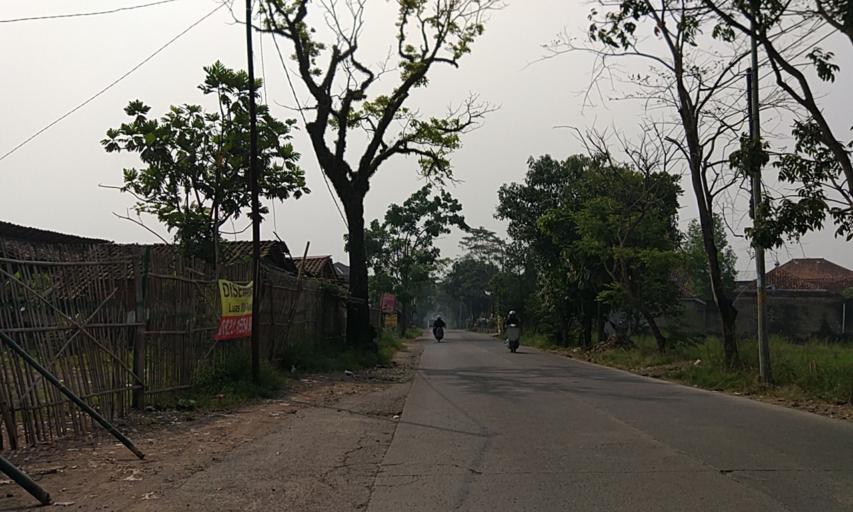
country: ID
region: West Java
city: Soreang
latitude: -7.0377
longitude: 107.5514
